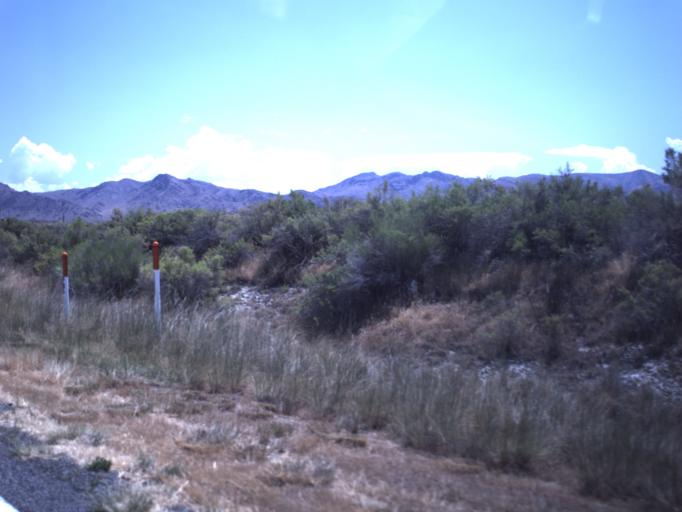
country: US
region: Utah
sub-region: Millard County
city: Delta
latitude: 39.5308
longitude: -112.3381
